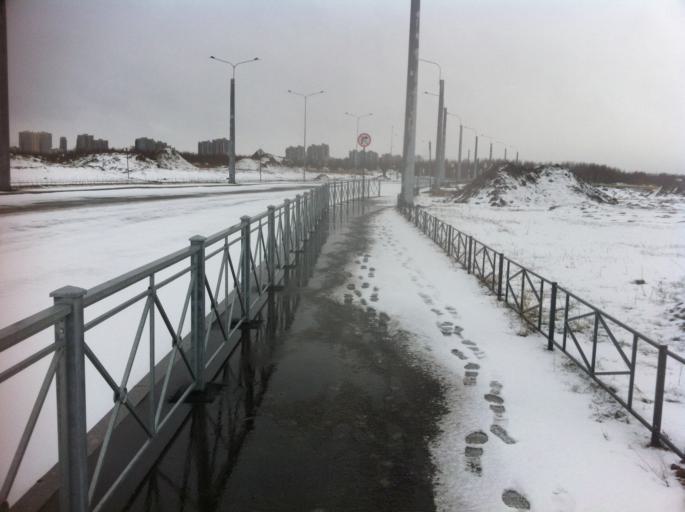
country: RU
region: St.-Petersburg
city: Sosnovaya Polyana
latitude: 59.8665
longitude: 30.1519
